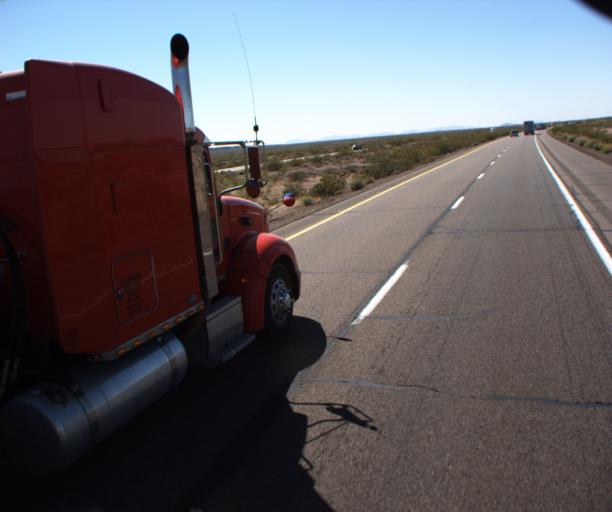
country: US
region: Arizona
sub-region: Maricopa County
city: Gila Bend
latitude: 32.8635
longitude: -113.1670
